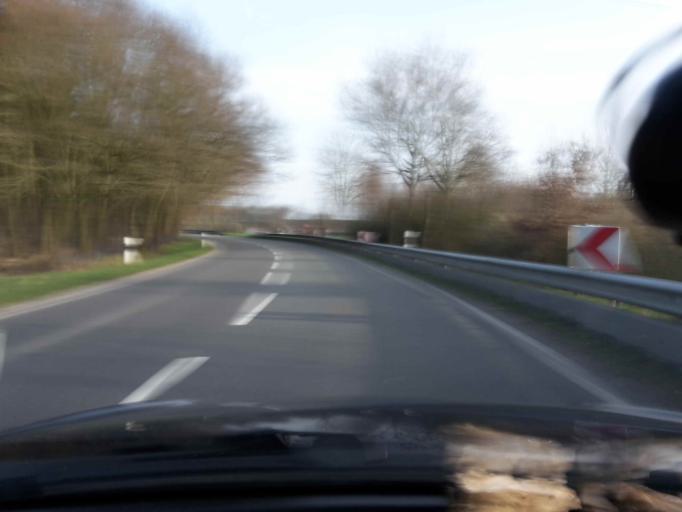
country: DE
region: Lower Saxony
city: Buchholz in der Nordheide
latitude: 53.3543
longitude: 9.8757
